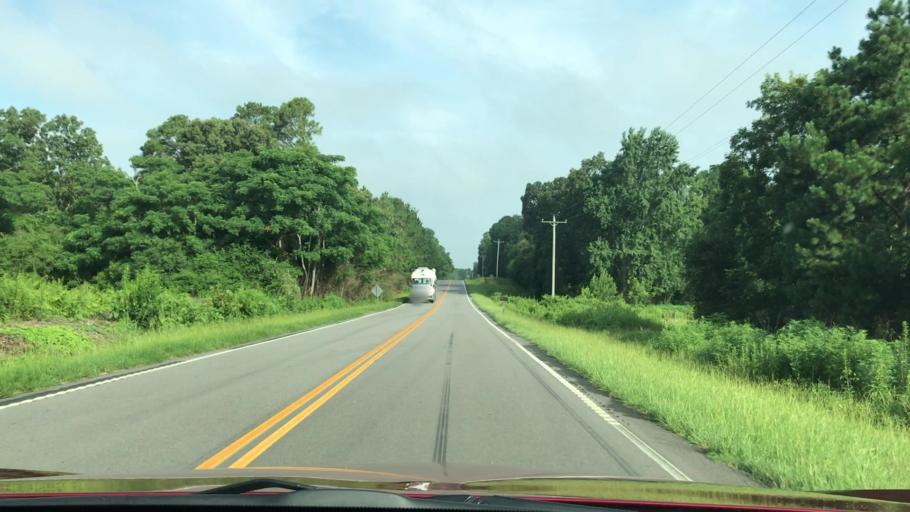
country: US
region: South Carolina
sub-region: Lexington County
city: Batesburg-Leesville
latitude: 33.7060
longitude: -81.4870
